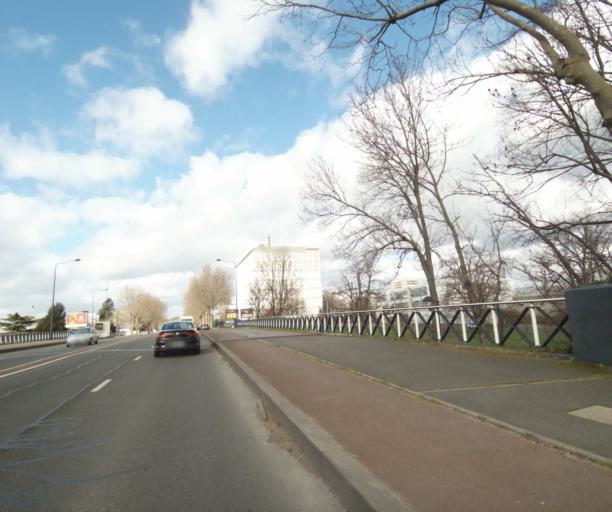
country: FR
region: Ile-de-France
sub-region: Departement de Seine-Saint-Denis
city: Saint-Denis
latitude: 48.9447
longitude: 2.3612
